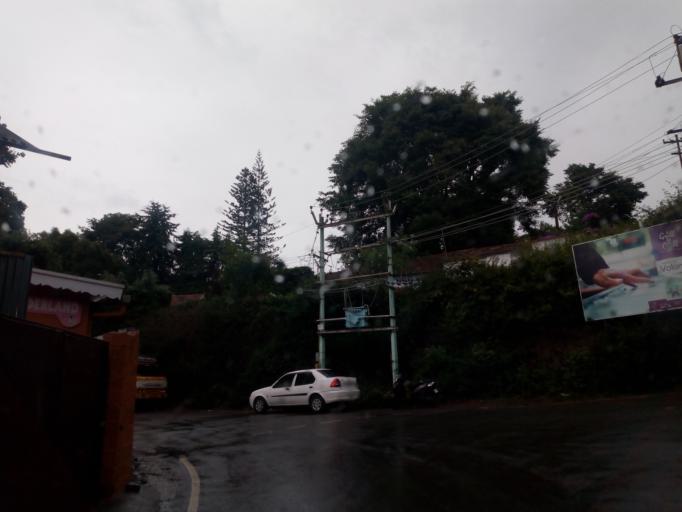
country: IN
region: Tamil Nadu
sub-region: Nilgiri
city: Wellington
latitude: 11.3491
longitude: 76.8026
